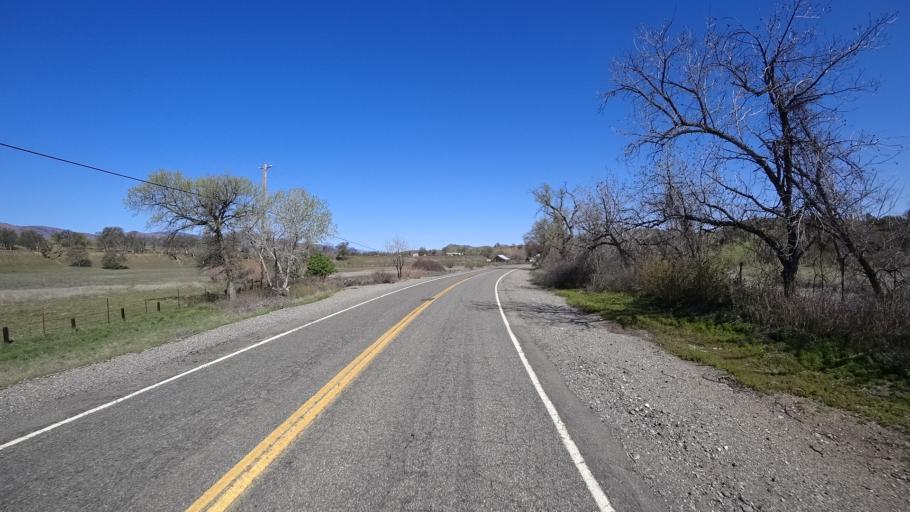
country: US
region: California
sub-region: Glenn County
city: Orland
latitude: 39.6724
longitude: -122.5268
